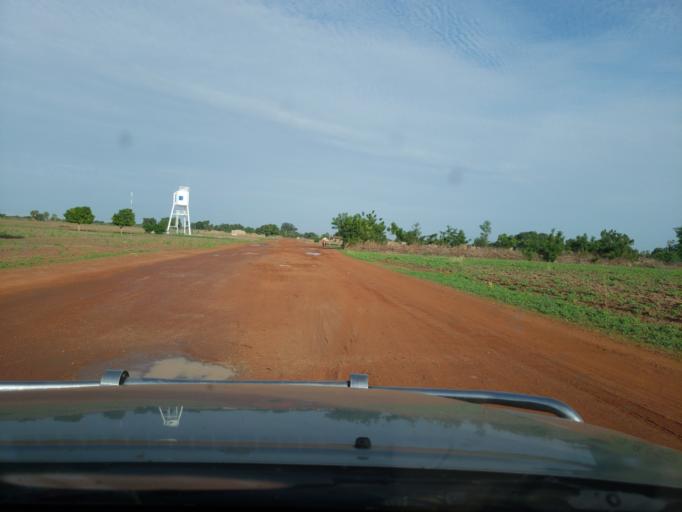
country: ML
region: Sikasso
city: Koutiala
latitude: 12.4232
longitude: -5.6751
